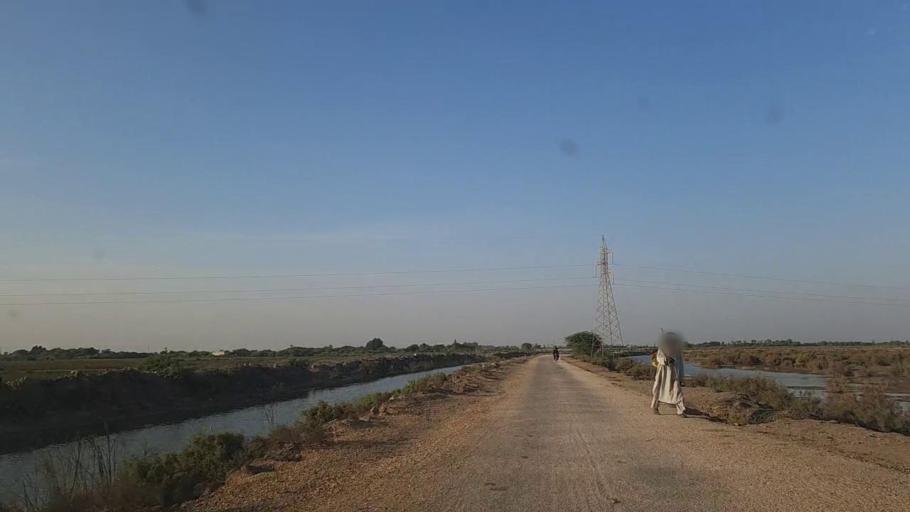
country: PK
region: Sindh
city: Mirpur Batoro
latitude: 24.6920
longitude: 68.2002
